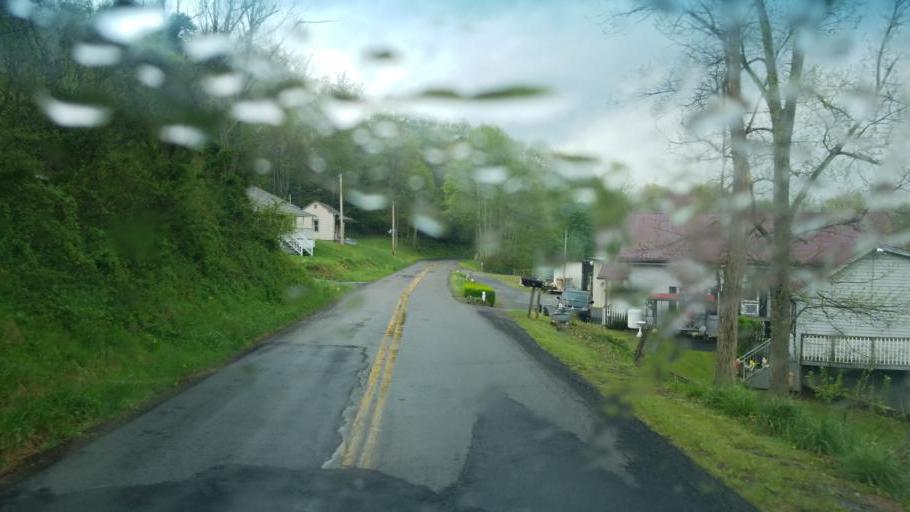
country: US
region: Virginia
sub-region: Smyth County
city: Adwolf
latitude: 36.7582
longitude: -81.5491
